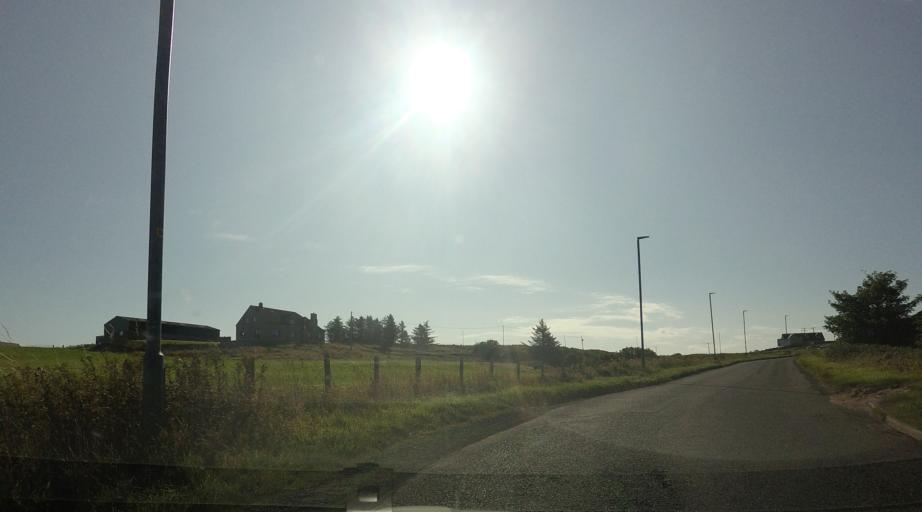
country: GB
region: Scotland
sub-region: Highland
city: Wick
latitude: 58.6376
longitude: -3.1601
